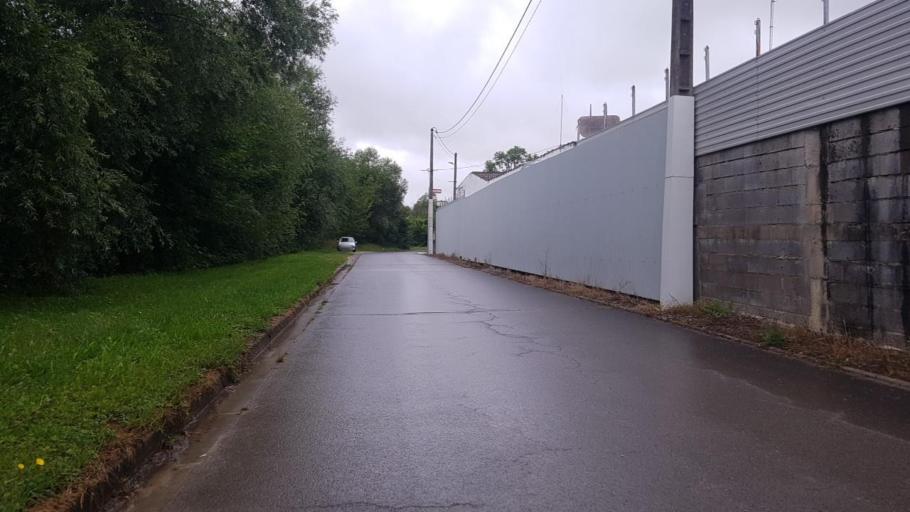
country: FR
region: Champagne-Ardenne
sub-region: Departement de la Marne
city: Vitry-le-Francois
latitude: 48.7508
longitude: 4.5713
